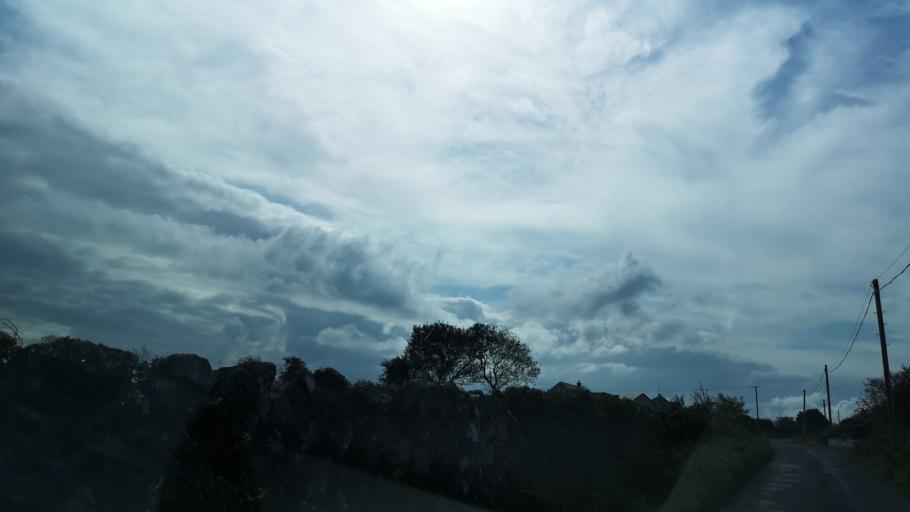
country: IE
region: Connaught
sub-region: County Galway
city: Athenry
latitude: 53.3106
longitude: -8.8075
